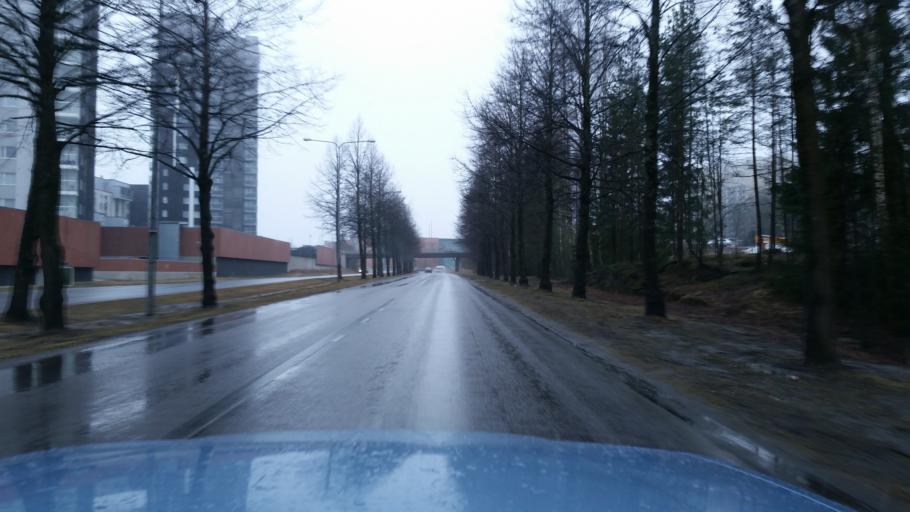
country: FI
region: Pirkanmaa
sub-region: Tampere
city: Tampere
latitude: 61.4574
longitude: 23.8469
